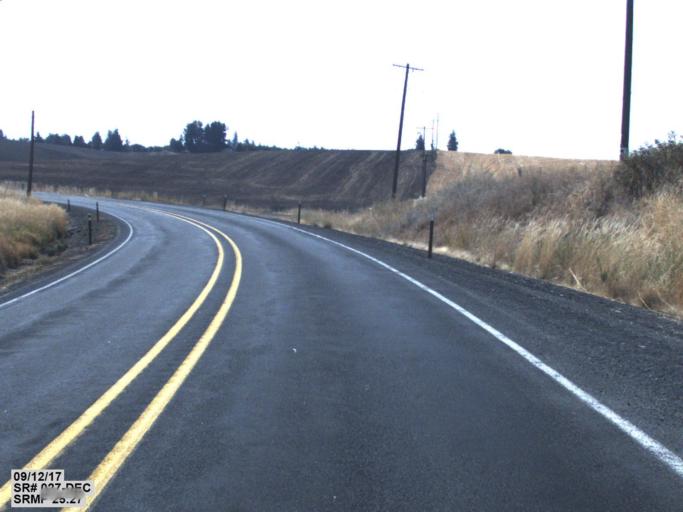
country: US
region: Washington
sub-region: Whitman County
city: Colfax
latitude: 47.0182
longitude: -117.1491
